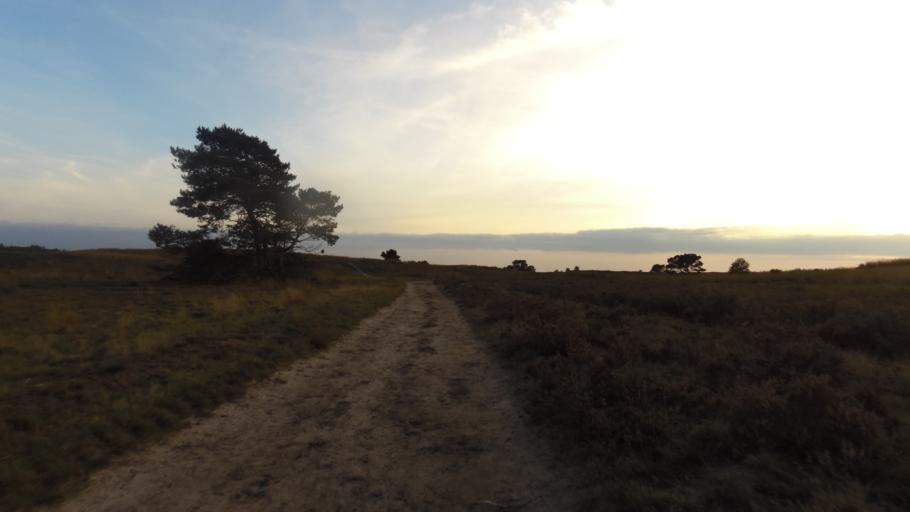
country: NL
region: Gelderland
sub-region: Gemeente Nunspeet
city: Nunspeet
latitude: 52.3291
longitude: 5.8122
